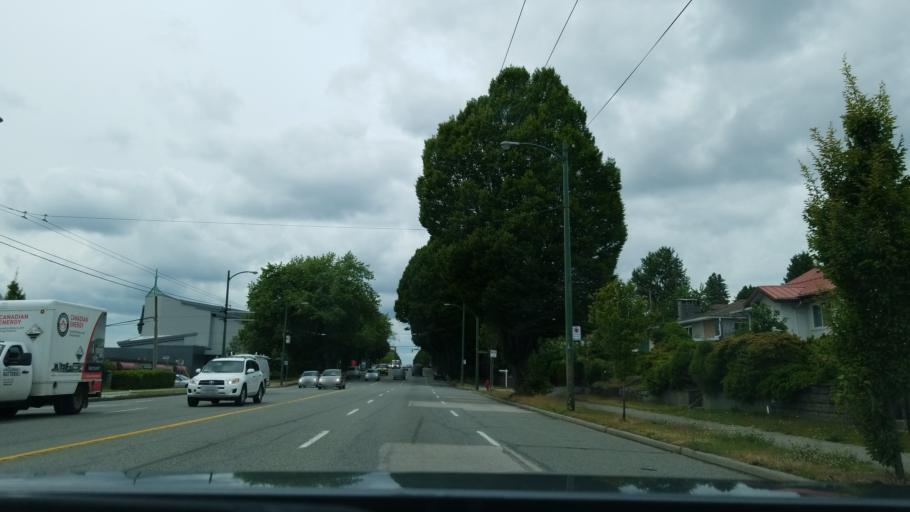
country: CA
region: British Columbia
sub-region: Fraser Valley Regional District
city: North Vancouver
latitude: 49.2620
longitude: -123.0461
